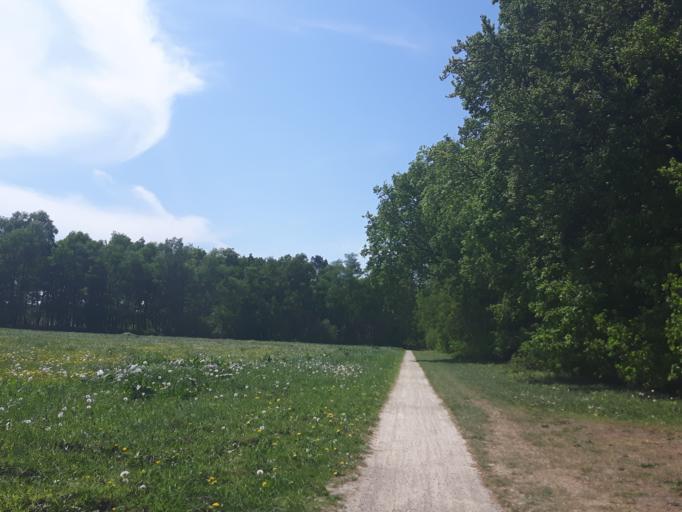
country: NL
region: Overijssel
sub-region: Gemeente Enschede
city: Enschede
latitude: 52.1552
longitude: 6.8781
